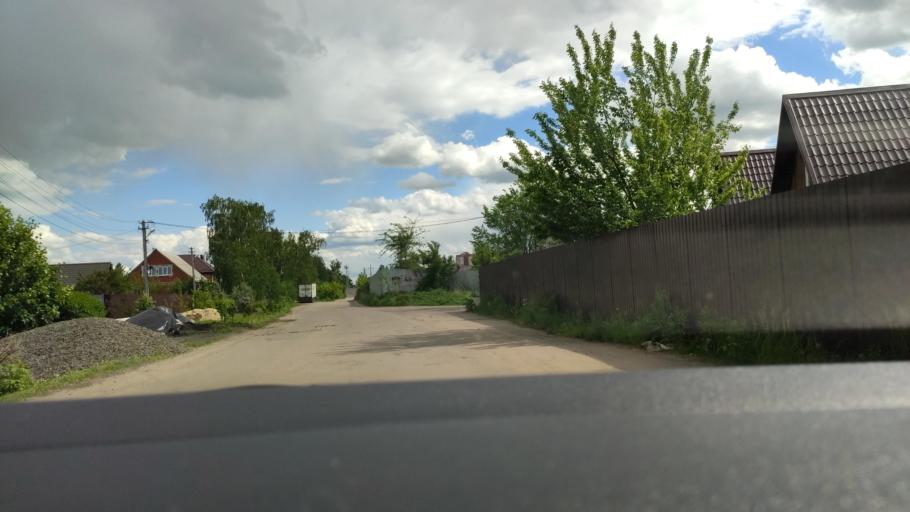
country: RU
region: Voronezj
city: Somovo
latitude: 51.6807
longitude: 39.3170
